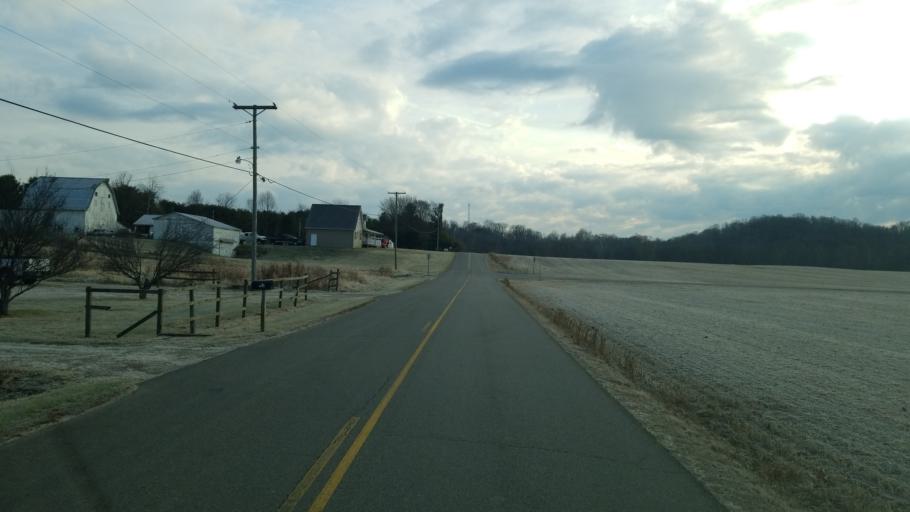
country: US
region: Ohio
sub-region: Ross County
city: Chillicothe
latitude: 39.2520
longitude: -82.8650
